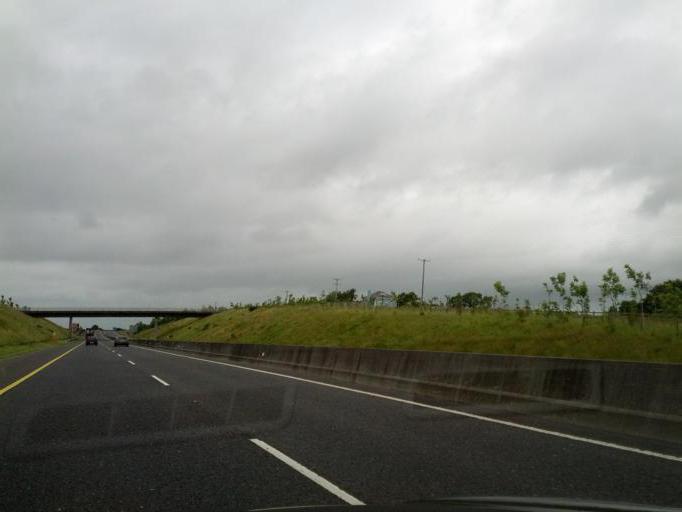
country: IE
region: Munster
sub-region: An Clar
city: Newmarket on Fergus
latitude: 52.8047
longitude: -8.9281
